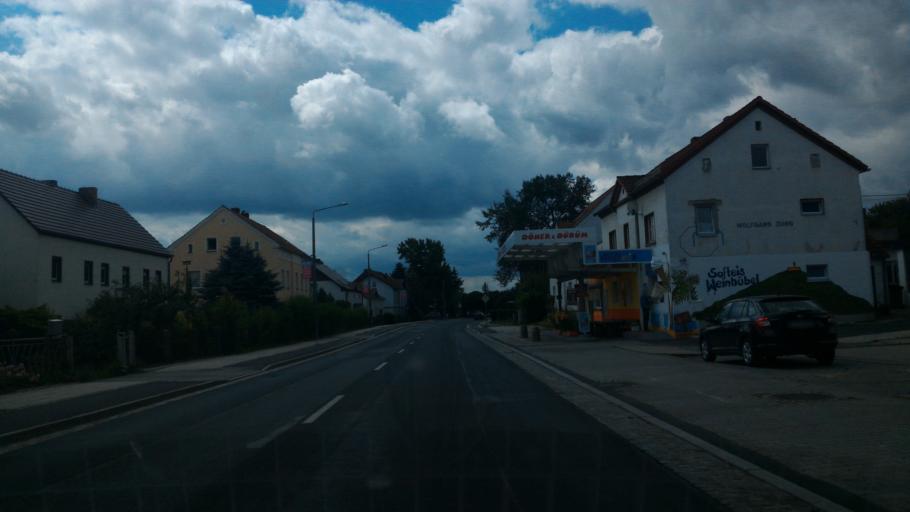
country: DE
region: Saxony
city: Goerlitz
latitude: 51.1199
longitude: 14.9817
